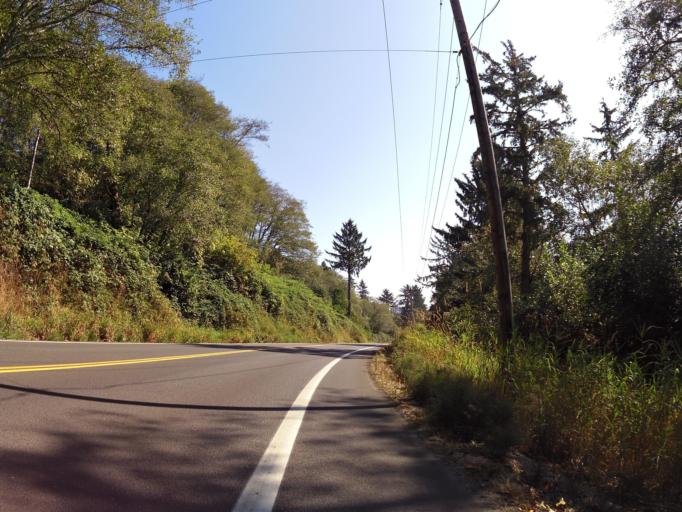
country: US
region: Oregon
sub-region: Tillamook County
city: Pacific City
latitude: 45.1890
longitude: -123.9488
